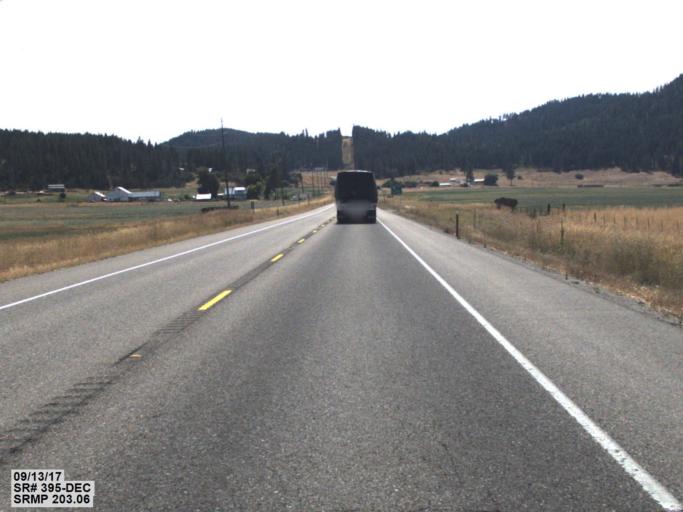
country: US
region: Washington
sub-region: Stevens County
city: Chewelah
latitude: 48.2173
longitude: -117.7154
